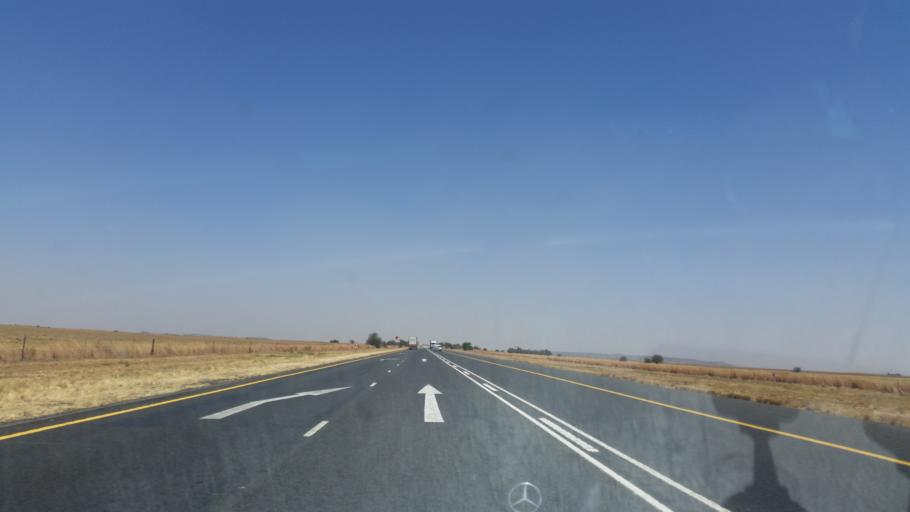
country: ZA
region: Orange Free State
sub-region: Lejweleputswa District Municipality
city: Winburg
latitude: -28.6463
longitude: 26.8819
